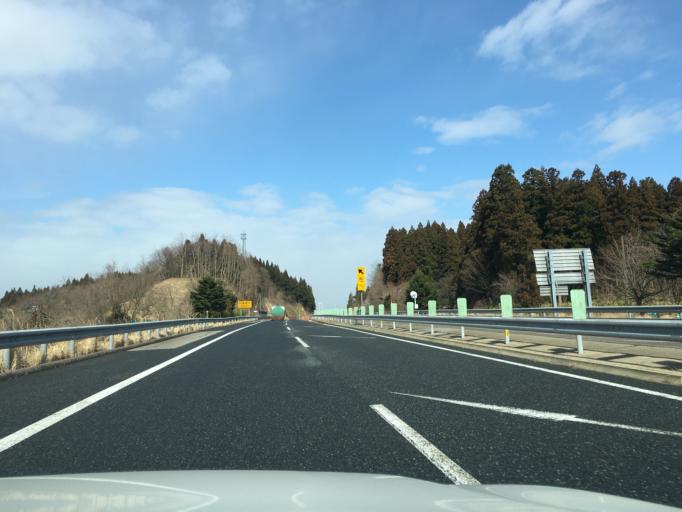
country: JP
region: Akita
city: Akita Shi
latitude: 39.7868
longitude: 140.1068
